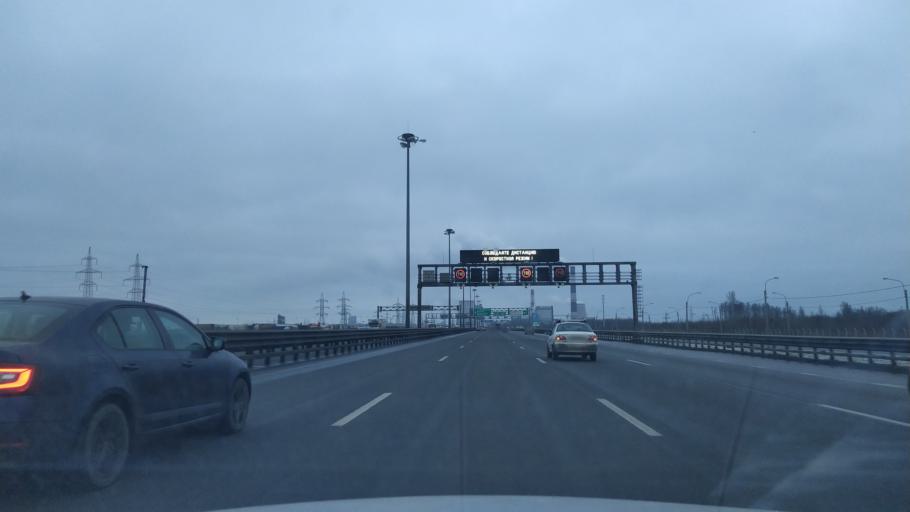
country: RU
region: St.-Petersburg
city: Obukhovo
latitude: 59.8220
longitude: 30.4187
